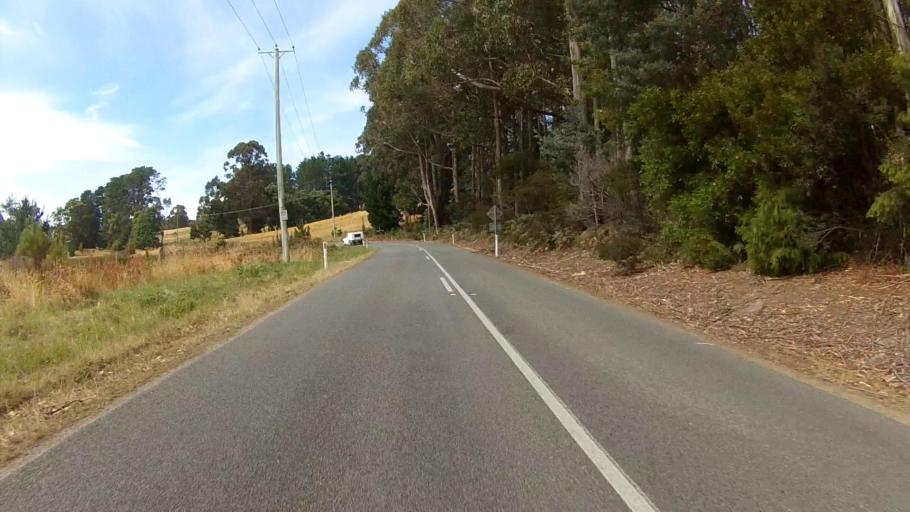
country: AU
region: Tasmania
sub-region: Kingborough
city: Kettering
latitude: -43.1927
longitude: 147.2476
